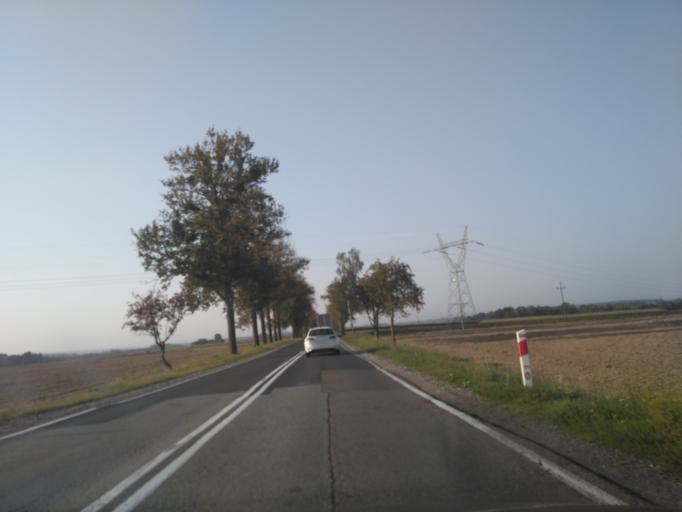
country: PL
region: Lublin Voivodeship
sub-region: Powiat krasnicki
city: Szastarka
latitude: 50.8155
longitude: 22.3191
